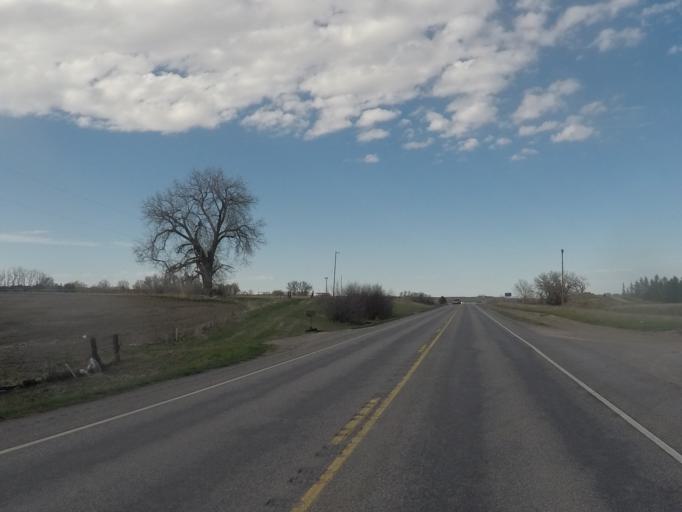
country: US
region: Montana
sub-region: Yellowstone County
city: Laurel
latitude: 45.5445
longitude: -108.8460
